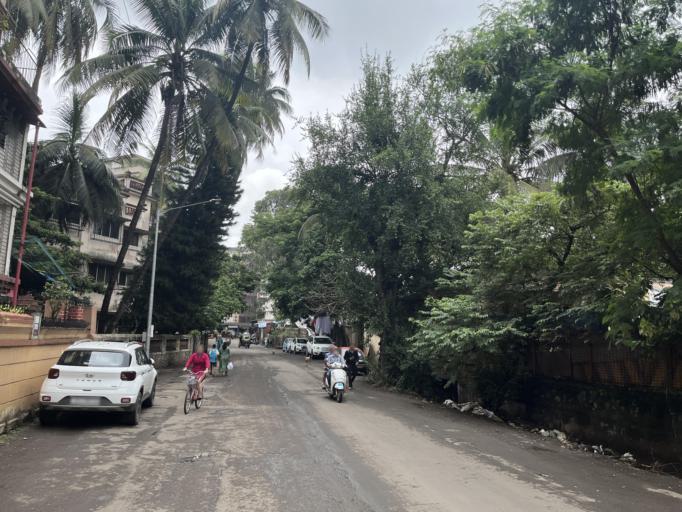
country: IN
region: Maharashtra
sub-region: Mumbai Suburban
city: Borivli
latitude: 19.2324
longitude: 72.8652
